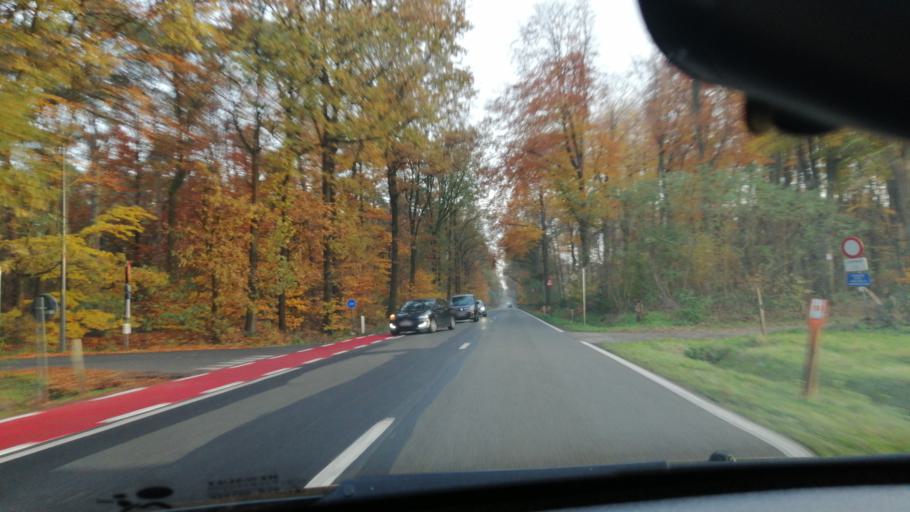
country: BE
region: Flanders
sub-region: Provincie Antwerpen
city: Oostmalle
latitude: 51.2912
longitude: 4.7472
